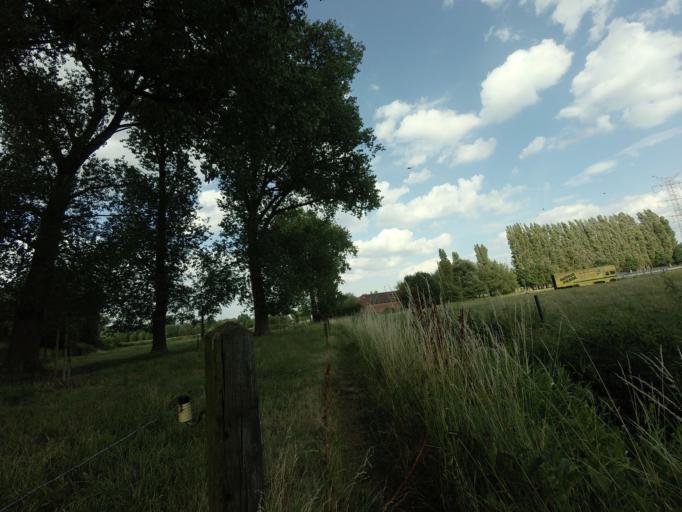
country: BE
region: Flanders
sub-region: Provincie Antwerpen
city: Kontich
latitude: 51.1165
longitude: 4.4583
